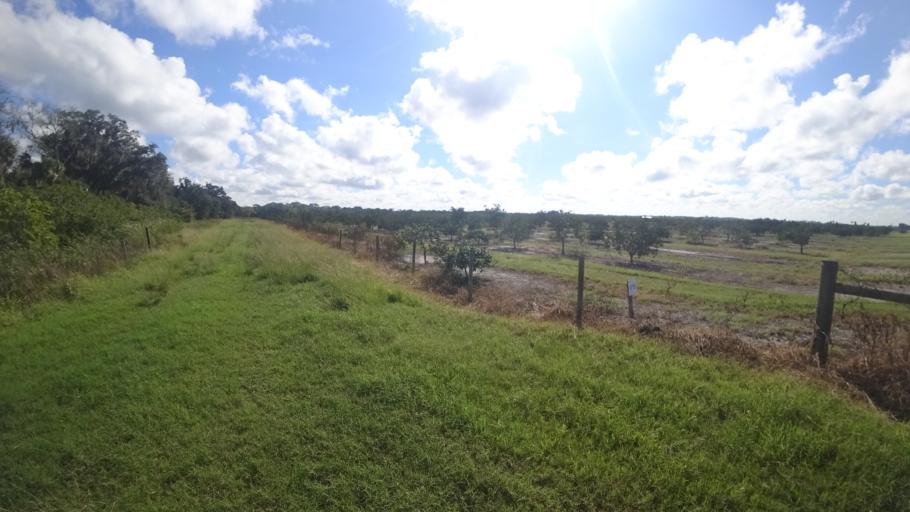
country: US
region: Florida
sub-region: Manatee County
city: Ellenton
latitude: 27.5958
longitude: -82.4745
